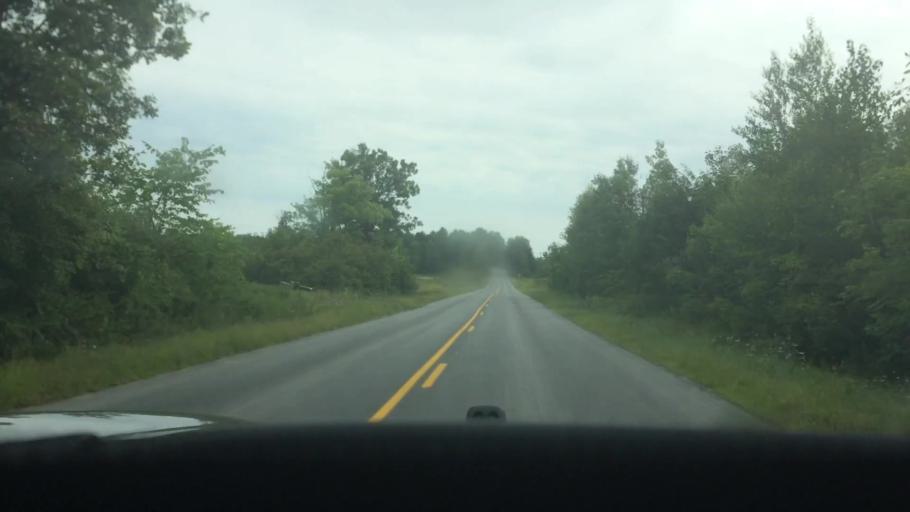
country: US
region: New York
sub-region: St. Lawrence County
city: Canton
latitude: 44.4977
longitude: -75.2989
